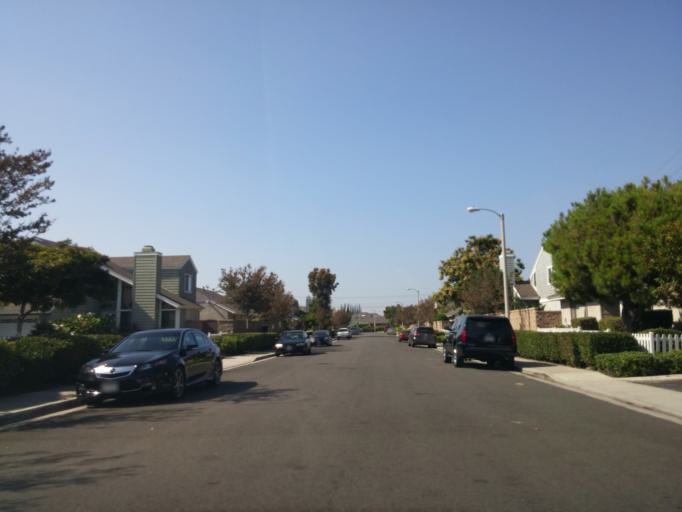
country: US
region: California
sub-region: Orange County
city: Irvine
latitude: 33.7008
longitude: -117.7974
